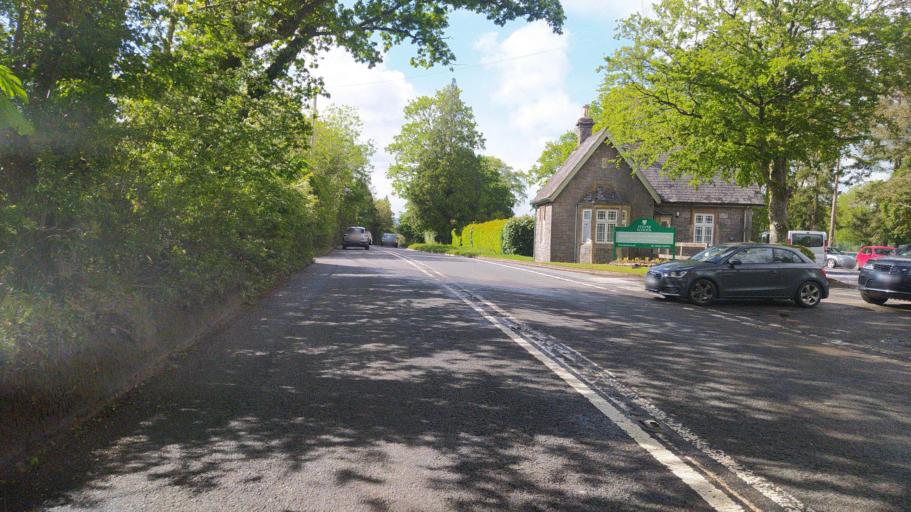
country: GB
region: England
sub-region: Devon
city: Newton Abbot
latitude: 50.5532
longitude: -3.6428
